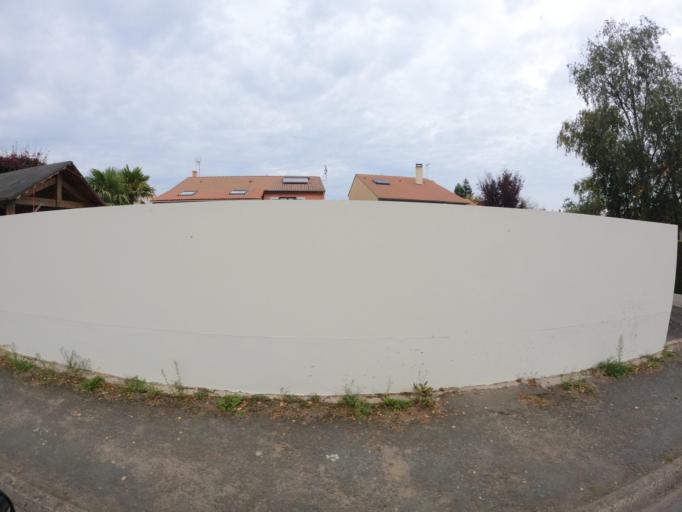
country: FR
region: Pays de la Loire
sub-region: Departement de Maine-et-Loire
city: Saint-Christophe-du-Bois
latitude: 47.0314
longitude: -0.9416
